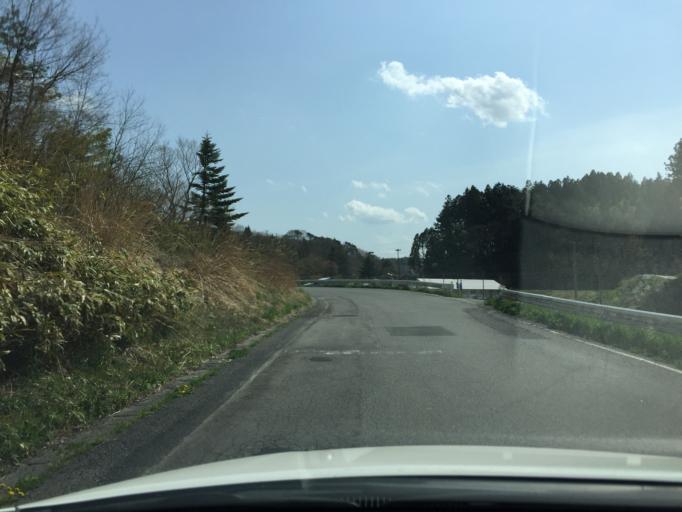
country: JP
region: Fukushima
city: Namie
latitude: 37.3981
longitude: 140.8015
